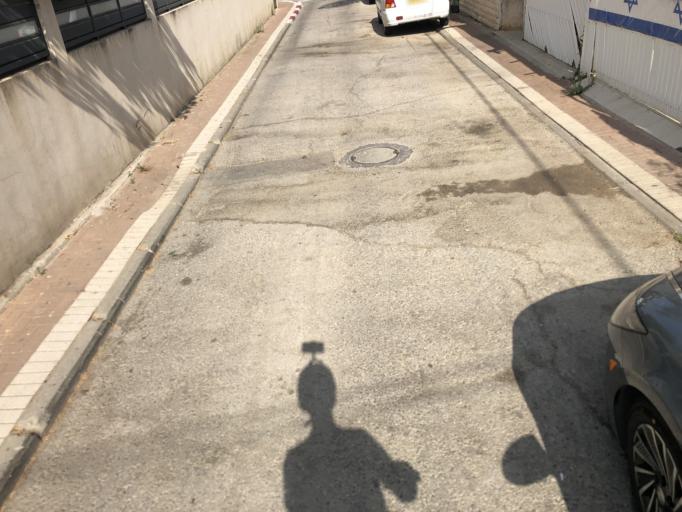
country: IL
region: Central District
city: Yehud
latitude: 32.0326
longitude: 34.8971
